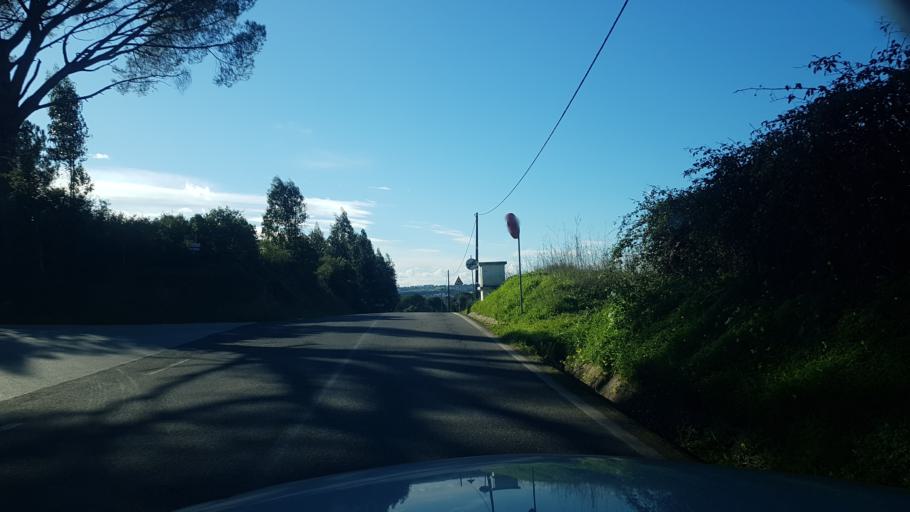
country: PT
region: Santarem
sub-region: Torres Novas
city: Riachos
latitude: 39.4773
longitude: -8.5060
